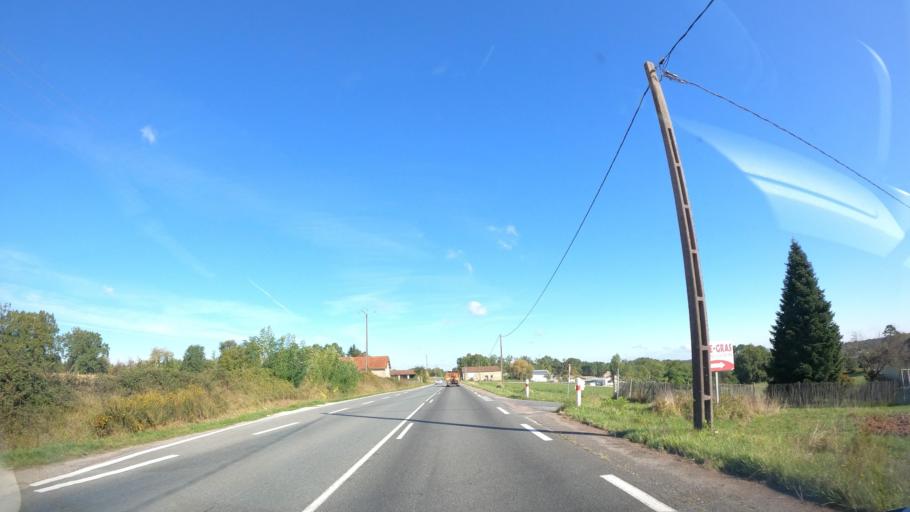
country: FR
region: Aquitaine
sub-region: Departement de la Dordogne
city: Notre-Dame-de-Sanilhac
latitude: 45.1093
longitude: 0.6926
